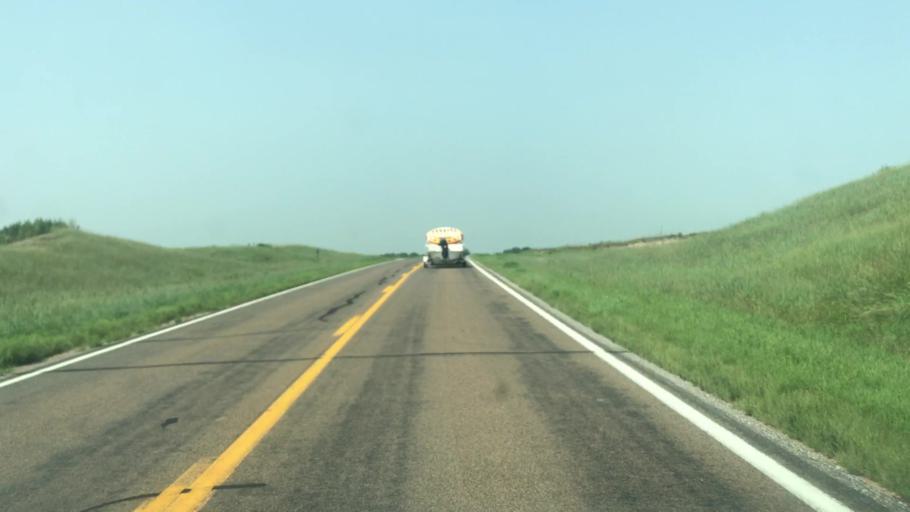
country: US
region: Nebraska
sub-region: Sherman County
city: Loup City
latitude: 41.2496
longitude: -98.9390
